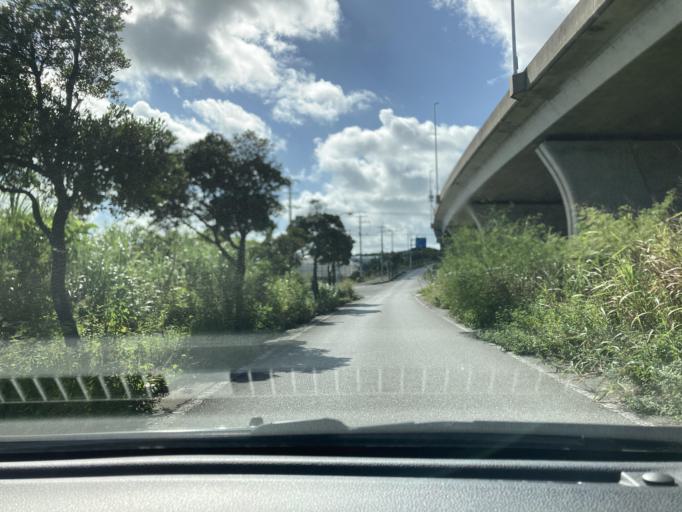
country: JP
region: Okinawa
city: Tomigusuku
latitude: 26.1810
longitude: 127.7293
